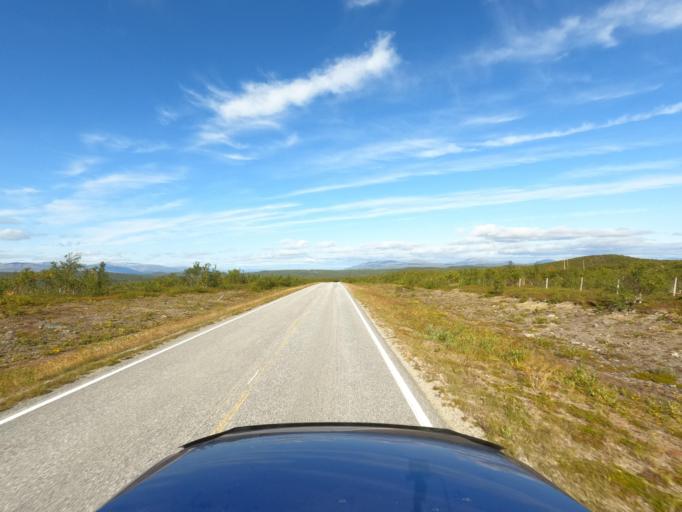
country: NO
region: Finnmark Fylke
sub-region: Karasjok
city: Karasjohka
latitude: 69.7224
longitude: 25.2365
